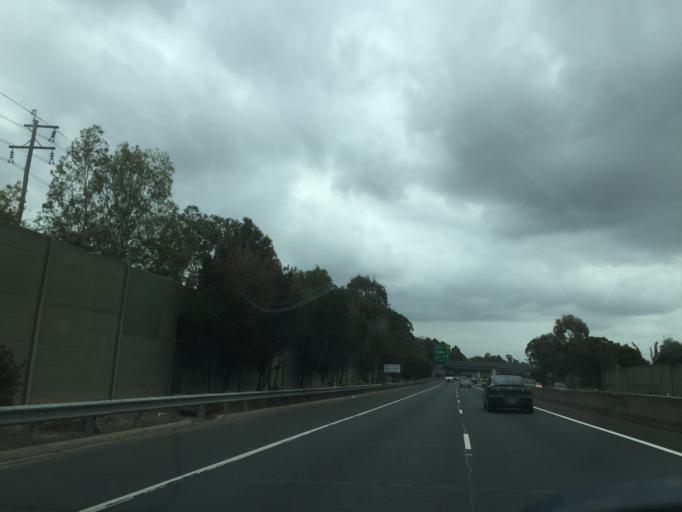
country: AU
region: New South Wales
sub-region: Parramatta
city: Northmead
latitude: -33.7725
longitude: 150.9772
